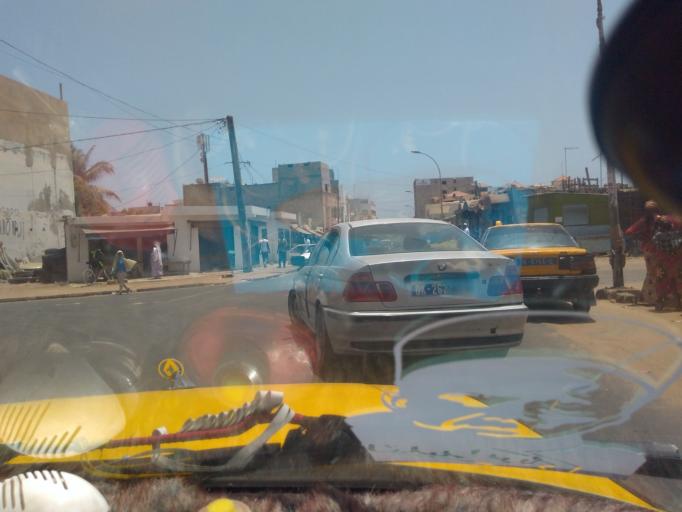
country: SN
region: Dakar
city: Grand Dakar
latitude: 14.7555
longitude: -17.4674
